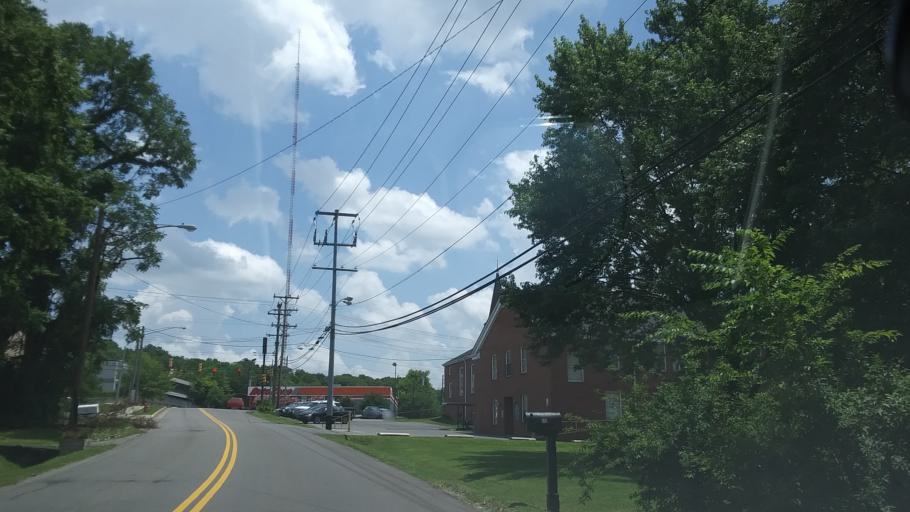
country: US
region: Tennessee
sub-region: Davidson County
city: Belle Meade
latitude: 36.1468
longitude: -86.8717
